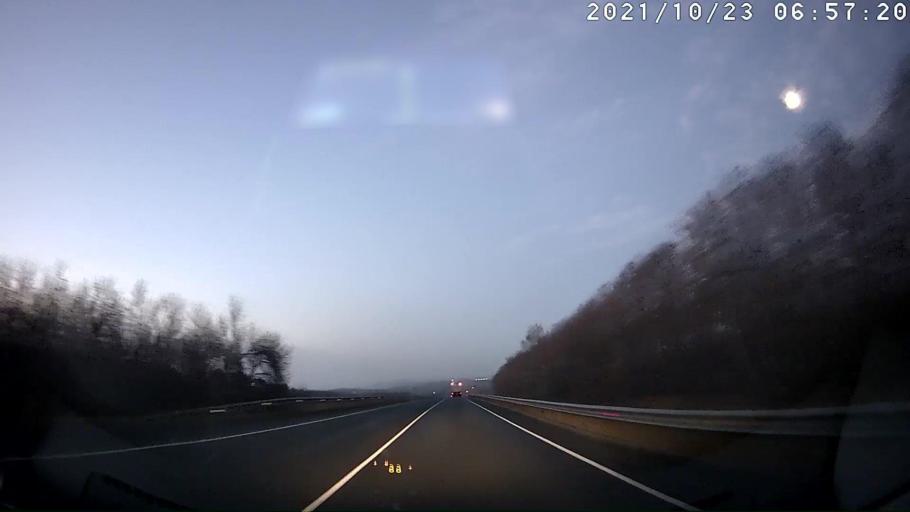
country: RU
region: Saratov
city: Dukhovnitskoye
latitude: 52.7103
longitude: 48.2651
